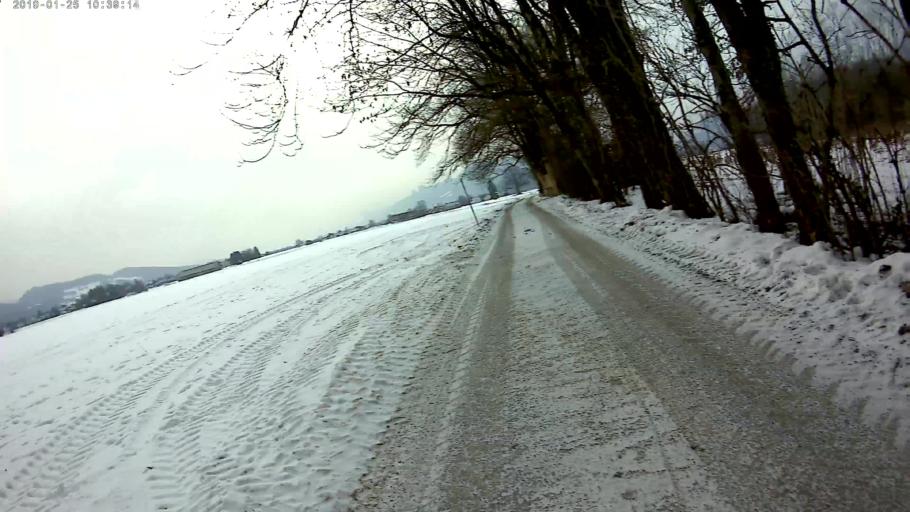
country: AT
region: Salzburg
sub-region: Politischer Bezirk Salzburg-Umgebung
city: Anif
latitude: 47.7546
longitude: 13.0488
